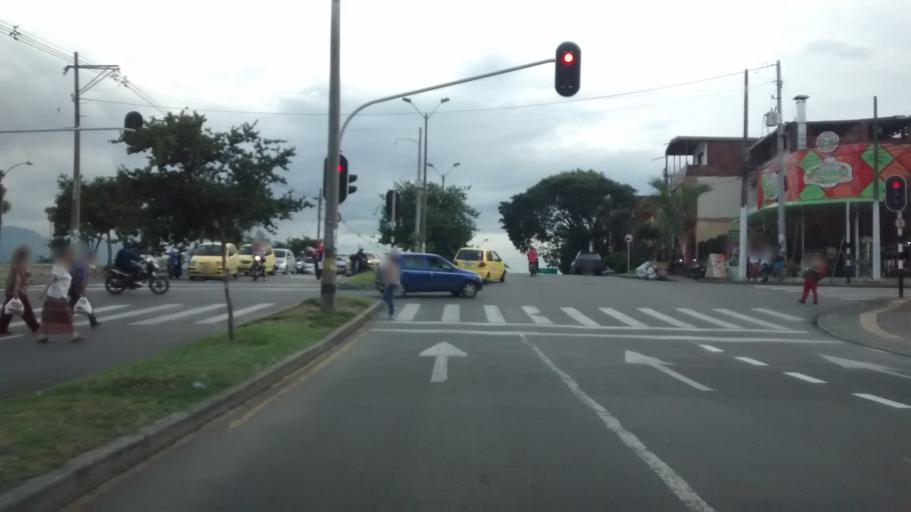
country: CO
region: Antioquia
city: Medellin
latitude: 6.2920
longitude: -75.5695
